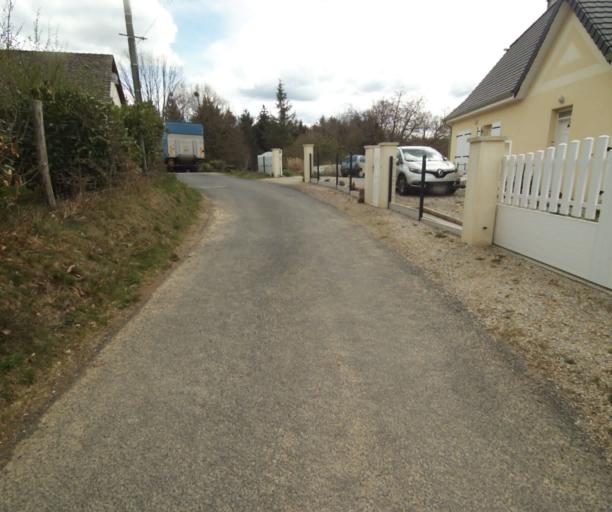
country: FR
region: Limousin
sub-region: Departement de la Correze
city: Laguenne
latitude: 45.2134
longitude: 1.8674
